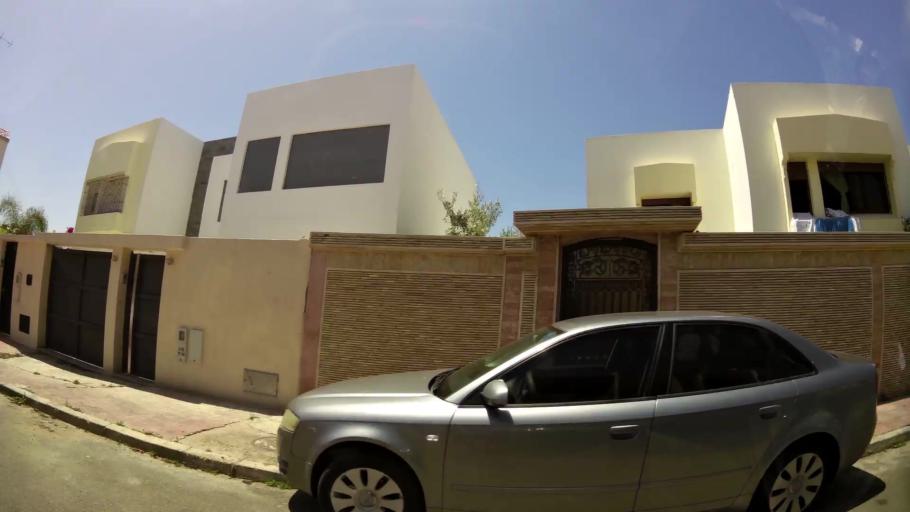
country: MA
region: Souss-Massa-Draa
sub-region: Agadir-Ida-ou-Tnan
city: Agadir
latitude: 30.4299
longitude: -9.5920
